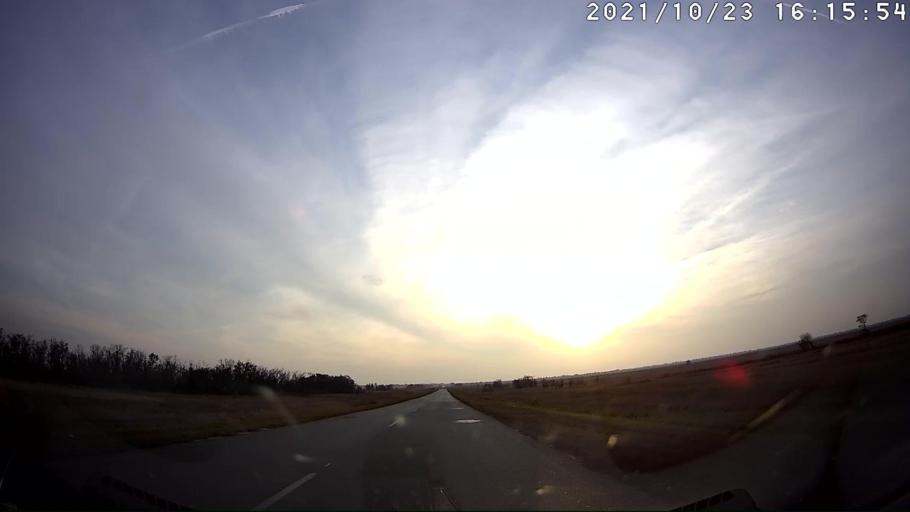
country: RU
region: Volgograd
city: Kotel'nikovo
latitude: 47.9294
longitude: 43.5863
